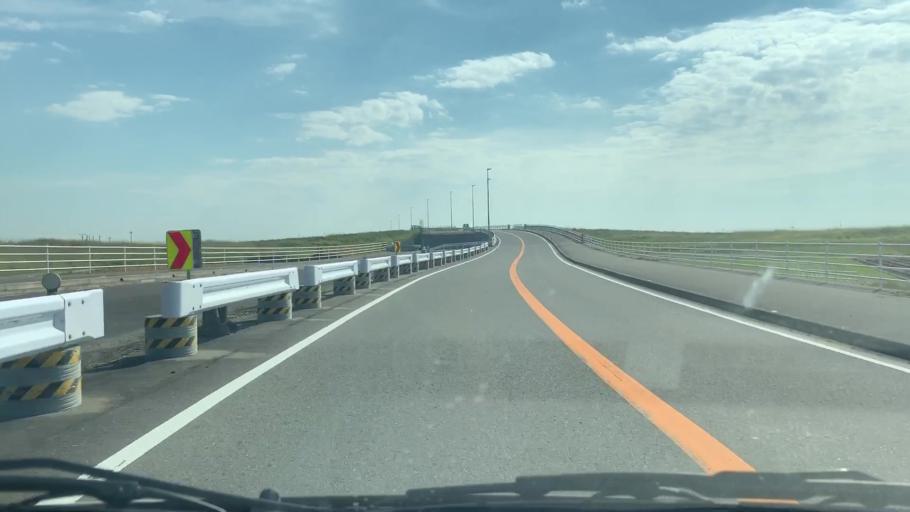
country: JP
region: Saga Prefecture
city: Saga-shi
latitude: 33.2235
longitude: 130.1912
